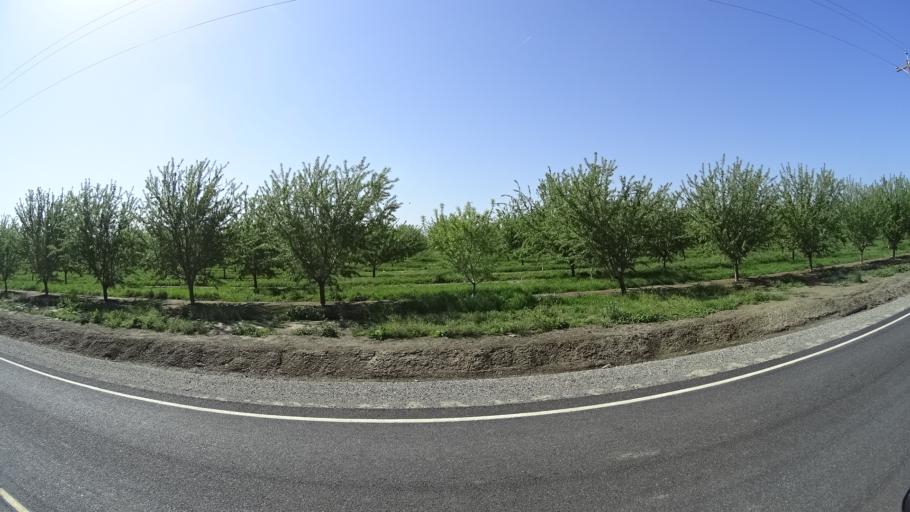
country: US
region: California
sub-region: Glenn County
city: Hamilton City
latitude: 39.6597
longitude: -122.0488
